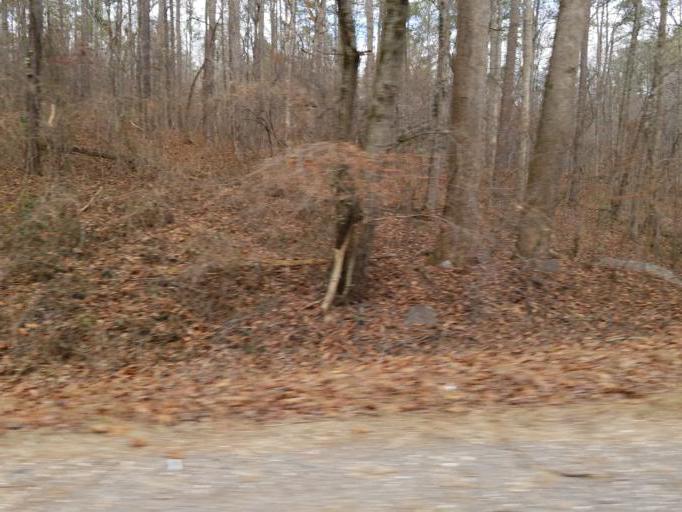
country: US
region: Georgia
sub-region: Pickens County
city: Jasper
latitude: 34.4907
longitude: -84.4247
